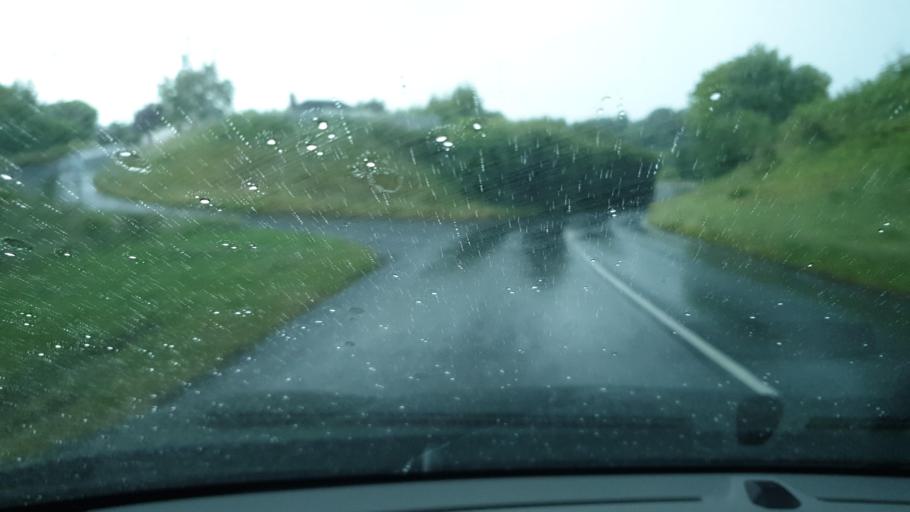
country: IE
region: Leinster
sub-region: An Mhi
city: Navan
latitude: 53.6311
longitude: -6.6655
